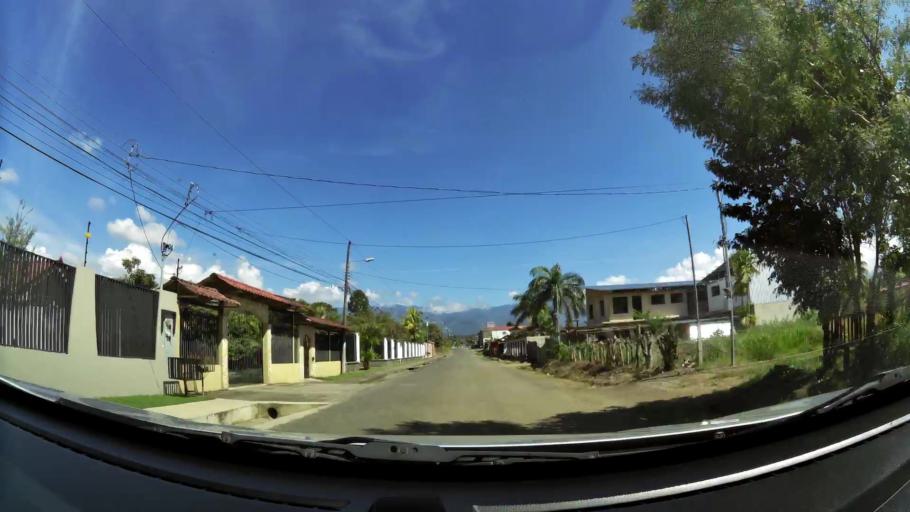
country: CR
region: San Jose
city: San Isidro
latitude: 9.3549
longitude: -83.6922
